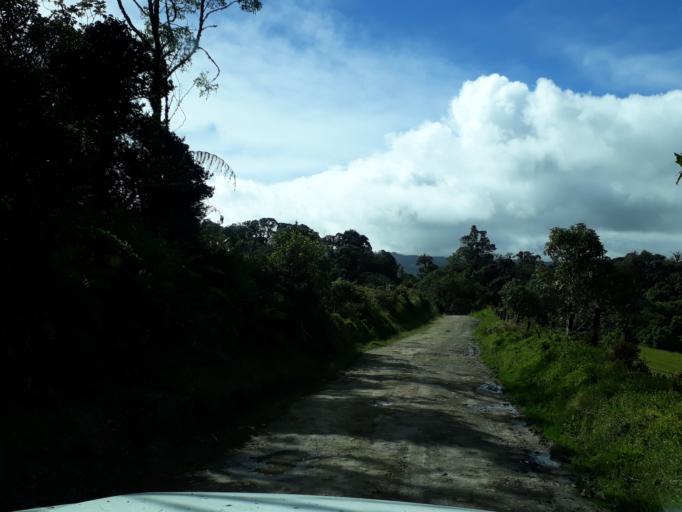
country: CO
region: Cundinamarca
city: Guasca
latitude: 4.7996
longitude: -73.7825
